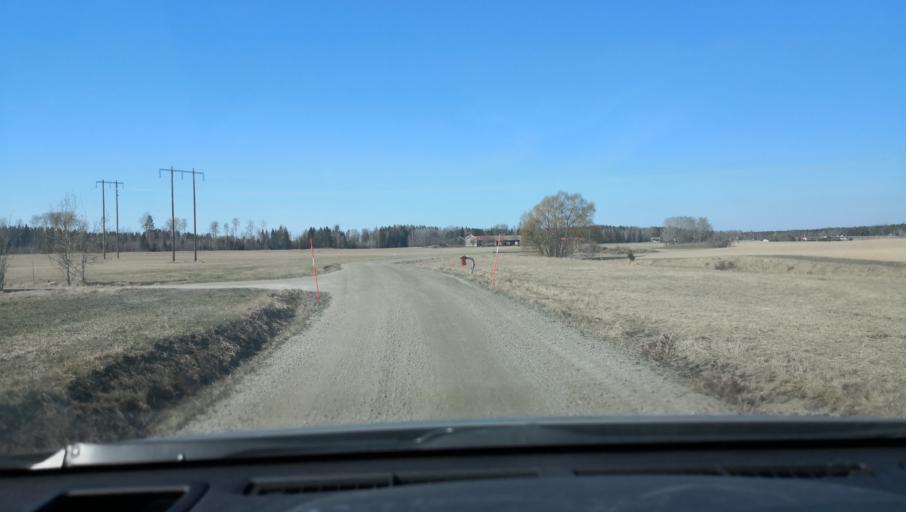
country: SE
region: Vaestmanland
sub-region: Sala Kommun
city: Sala
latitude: 59.8954
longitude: 16.5305
